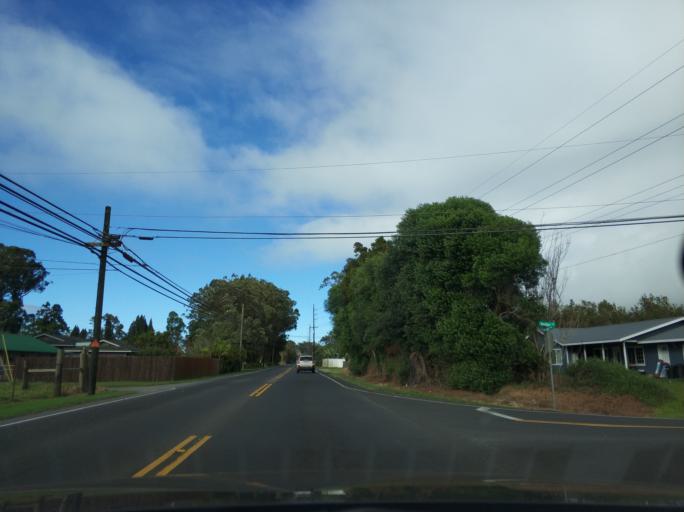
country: US
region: Hawaii
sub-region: Hawaii County
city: Waimea
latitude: 20.0367
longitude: -155.6238
